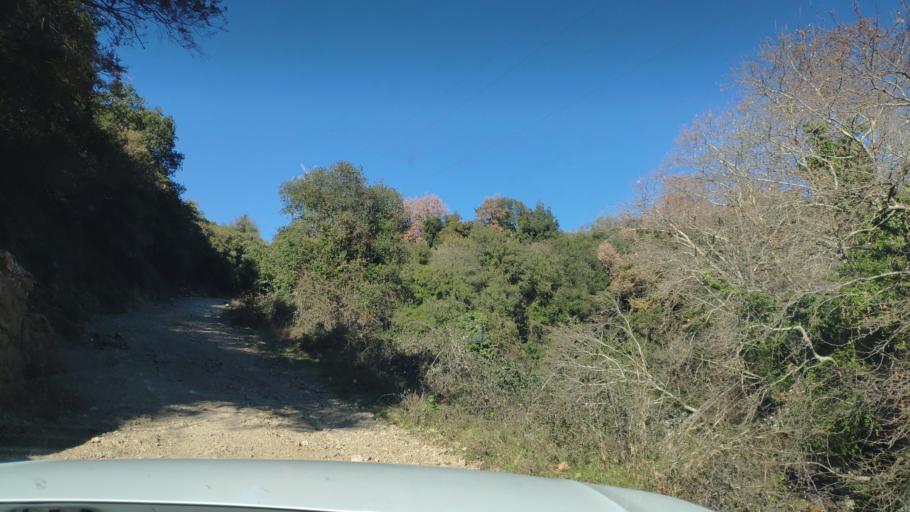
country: GR
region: West Greece
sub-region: Nomos Aitolias kai Akarnanias
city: Thermo
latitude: 38.5803
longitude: 21.6328
